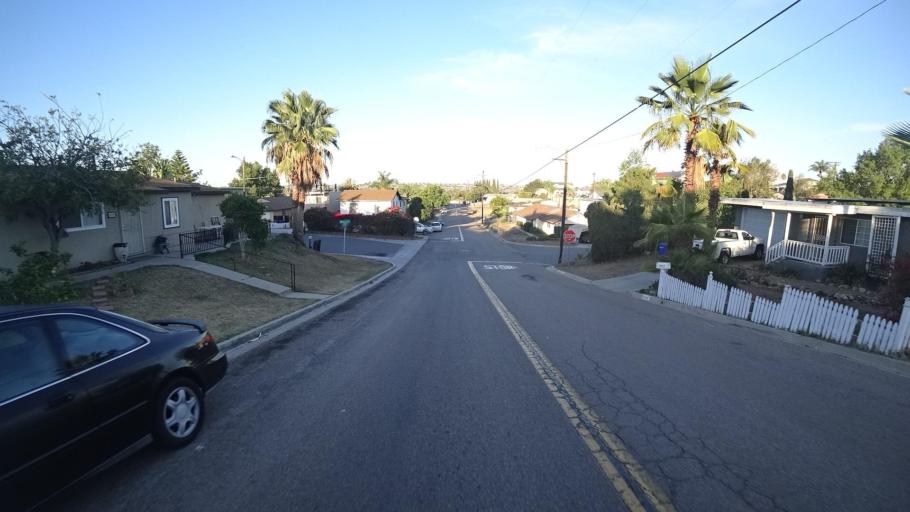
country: US
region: California
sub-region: San Diego County
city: La Presa
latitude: 32.7098
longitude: -116.9984
